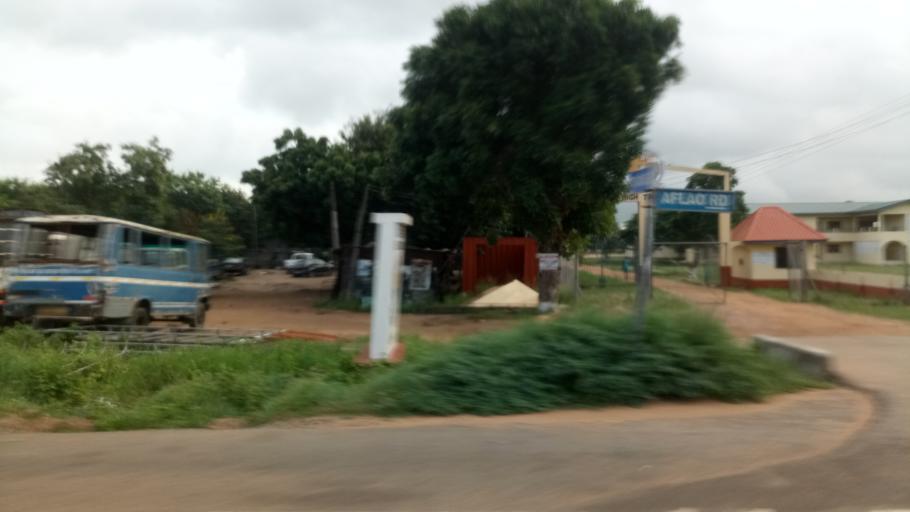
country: GH
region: Greater Accra
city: Tema
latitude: 5.8754
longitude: 0.3655
